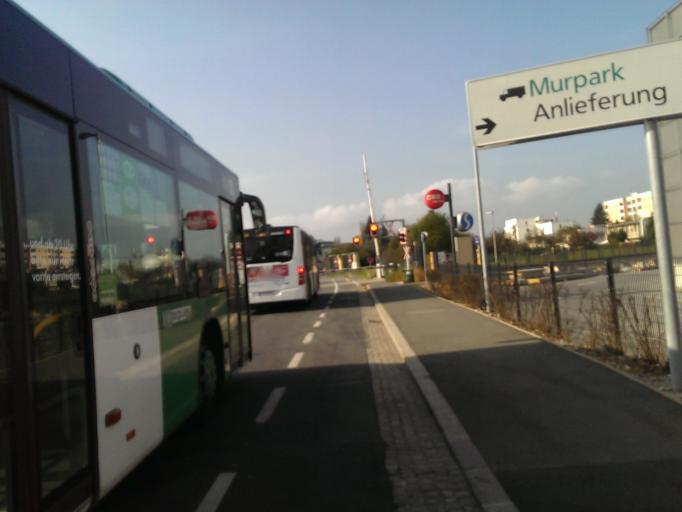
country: AT
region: Styria
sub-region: Politischer Bezirk Graz-Umgebung
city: Feldkirchen bei Graz
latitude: 47.0397
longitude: 15.4652
